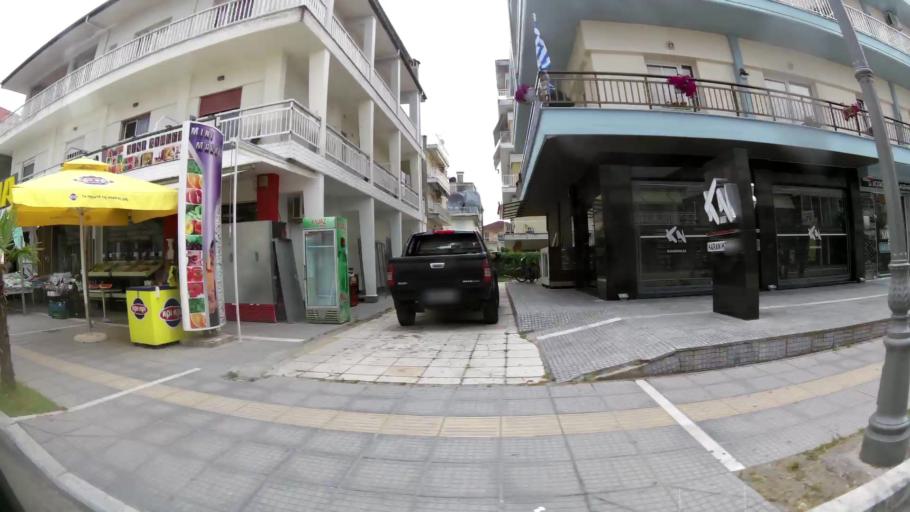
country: GR
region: Central Macedonia
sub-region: Nomos Pierias
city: Paralia
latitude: 40.2677
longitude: 22.5959
